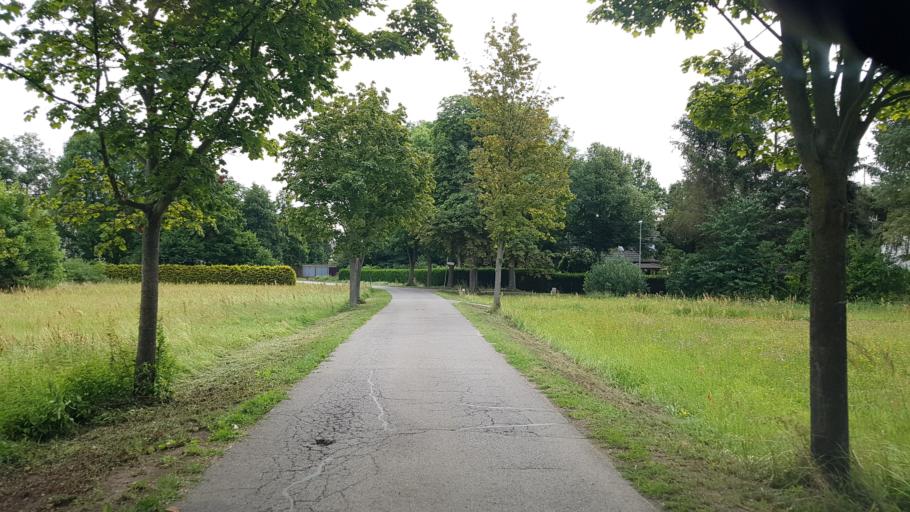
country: DE
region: Brandenburg
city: Drebkau
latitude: 51.6555
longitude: 14.2157
